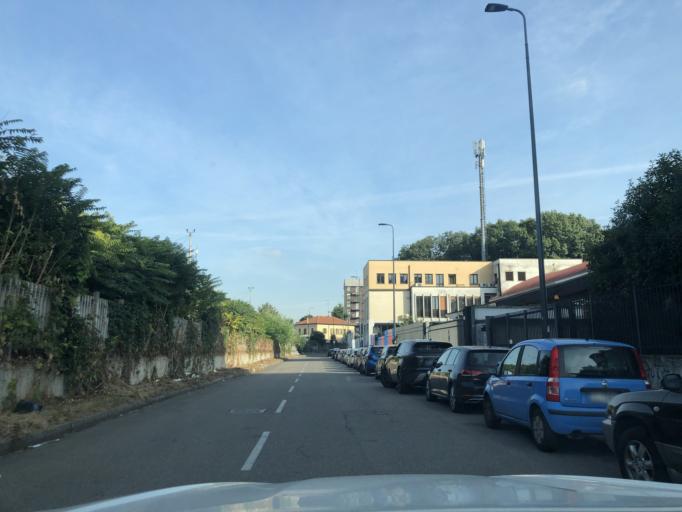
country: IT
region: Lombardy
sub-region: Citta metropolitana di Milano
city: Bresso
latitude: 45.5074
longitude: 9.1717
